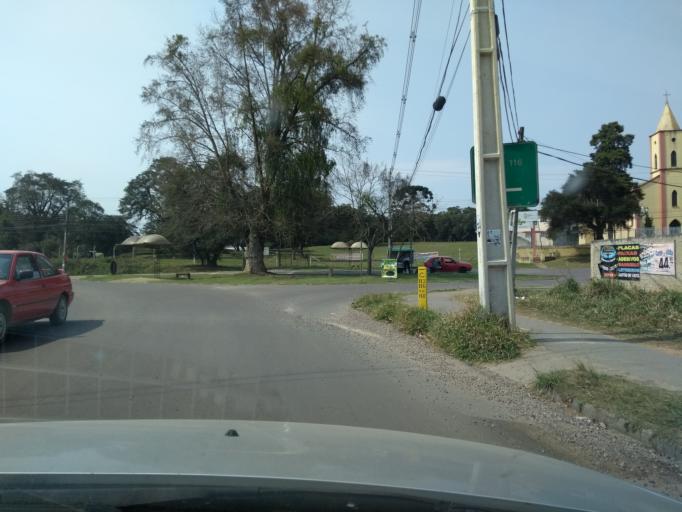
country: BR
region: Parana
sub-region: Araucaria
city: Araucaria
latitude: -25.6192
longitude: -49.3478
